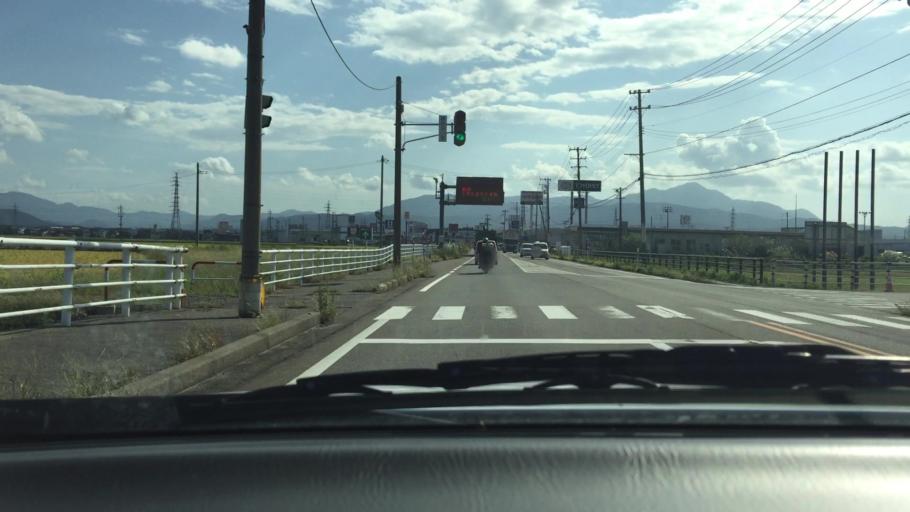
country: JP
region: Niigata
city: Kashiwazaki
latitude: 37.3832
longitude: 138.5830
